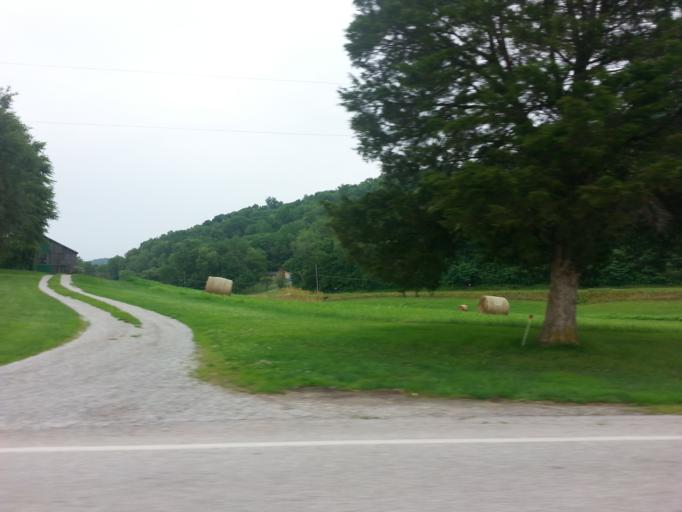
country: US
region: Ohio
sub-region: Brown County
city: Ripley
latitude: 38.7129
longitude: -83.8227
